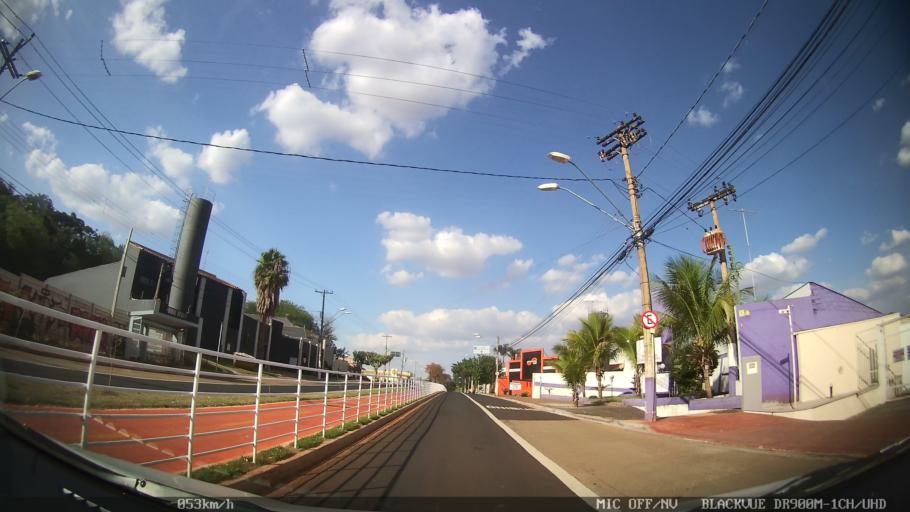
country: BR
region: Sao Paulo
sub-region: Ribeirao Preto
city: Ribeirao Preto
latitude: -21.1747
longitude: -47.8379
